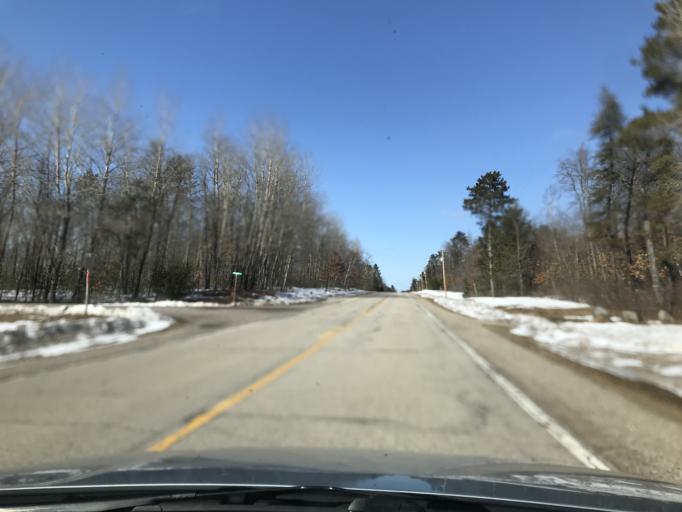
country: US
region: Wisconsin
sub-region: Marinette County
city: Niagara
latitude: 45.3546
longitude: -88.1010
